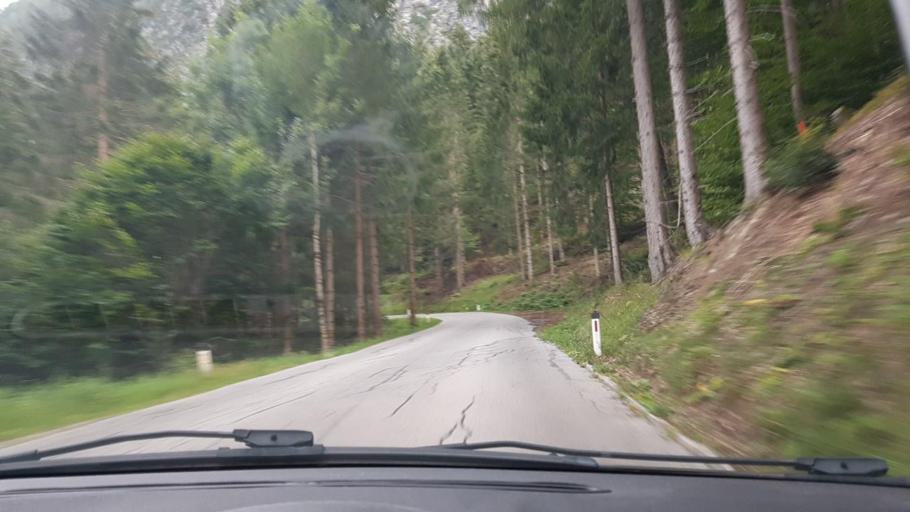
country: AT
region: Tyrol
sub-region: Politischer Bezirk Lienz
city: Tristach
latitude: 46.8112
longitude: 12.7899
